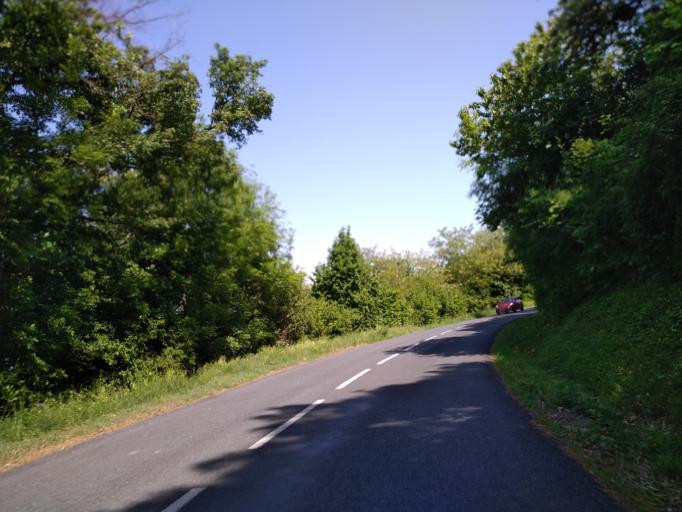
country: FR
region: Rhone-Alpes
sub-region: Departement du Rhone
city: Limonest
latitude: 45.8314
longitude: 4.8073
